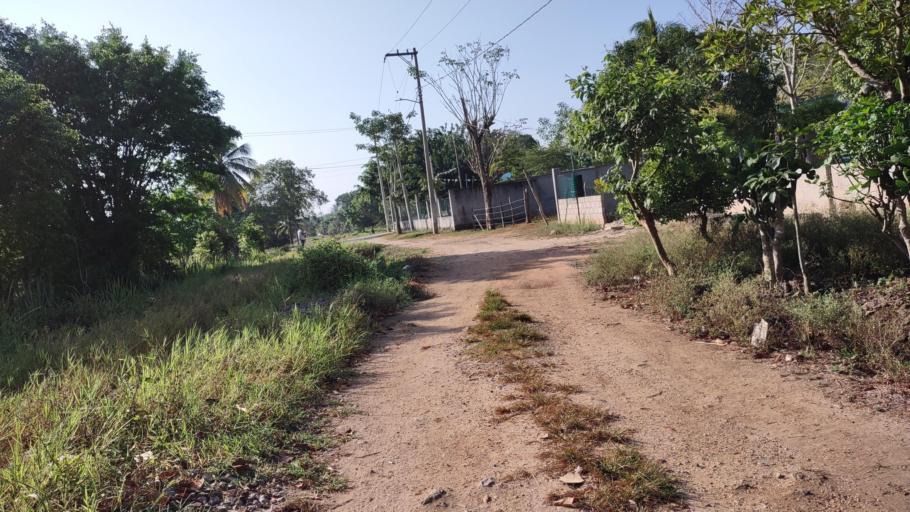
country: MX
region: Veracruz
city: Las Choapas
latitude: 17.8736
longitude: -94.0906
